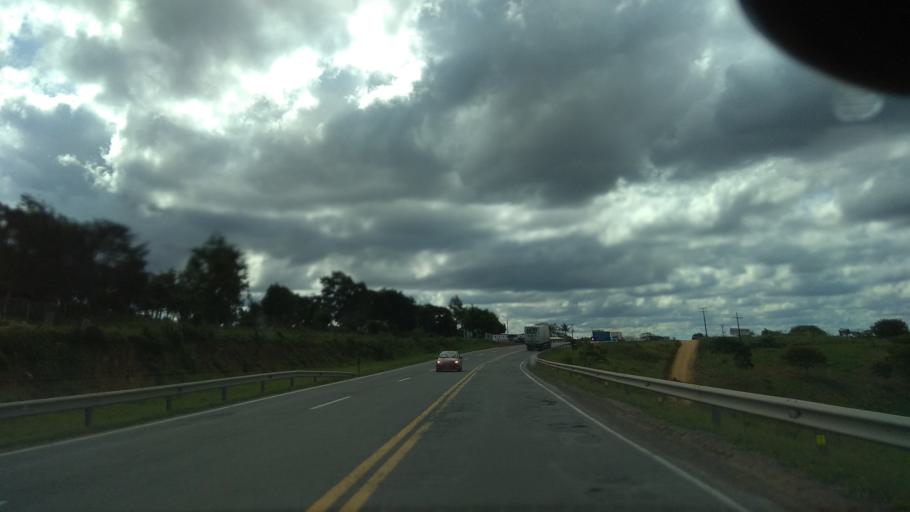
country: BR
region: Bahia
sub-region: Santa Ines
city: Santa Ines
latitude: -13.0940
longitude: -39.9629
